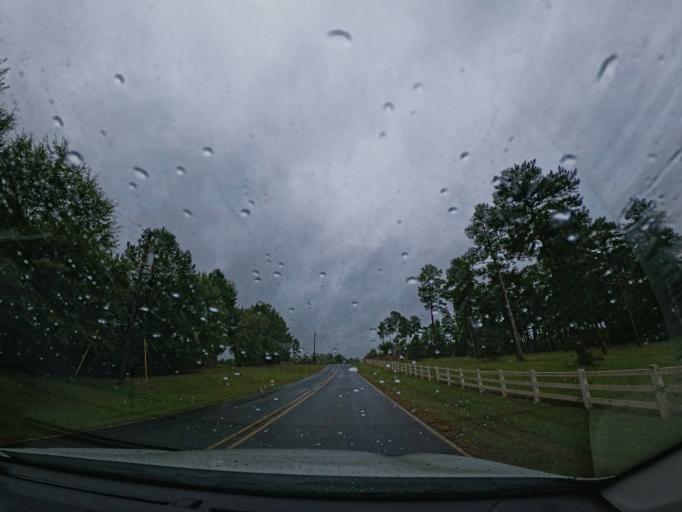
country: US
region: Louisiana
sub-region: Webster Parish
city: Minden
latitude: 32.6452
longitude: -93.2681
